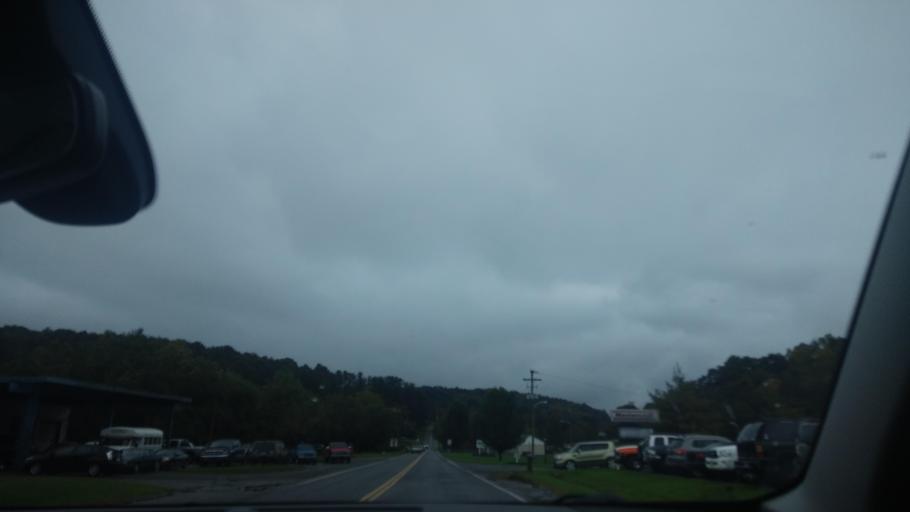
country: US
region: Virginia
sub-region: City of Galax
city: Galax
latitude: 36.6437
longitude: -80.9191
